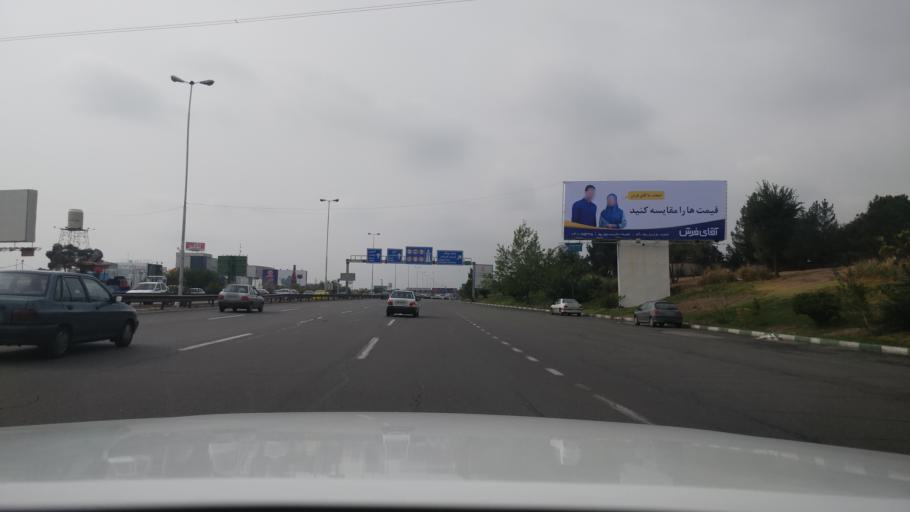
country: IR
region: Tehran
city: Shahr-e Qods
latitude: 35.7151
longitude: 51.2463
